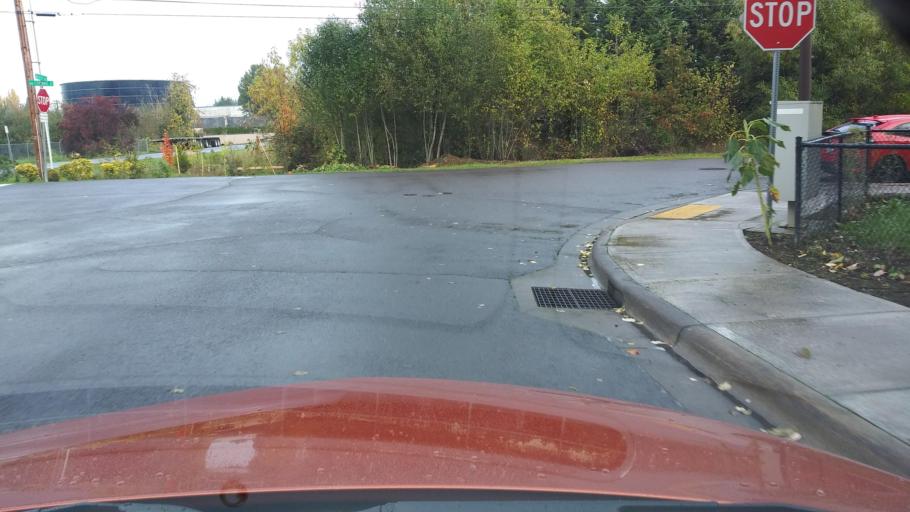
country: US
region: Oregon
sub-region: Washington County
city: North Plains
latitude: 45.5967
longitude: -123.0069
